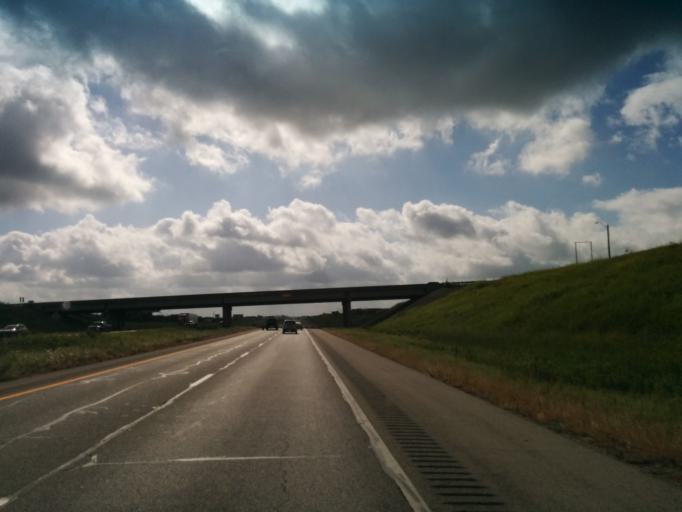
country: US
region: Texas
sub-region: Caldwell County
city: Luling
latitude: 29.6512
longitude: -97.6617
